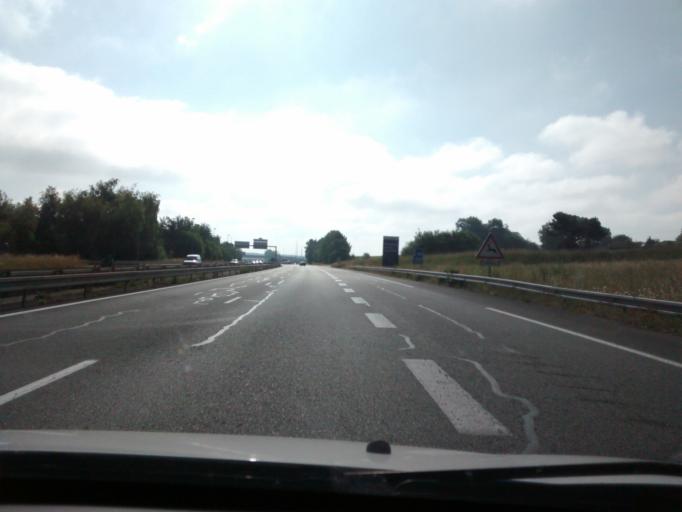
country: FR
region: Pays de la Loire
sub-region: Departement de la Mayenne
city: Saint-Pierre-la-Cour
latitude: 48.0828
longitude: -1.0365
